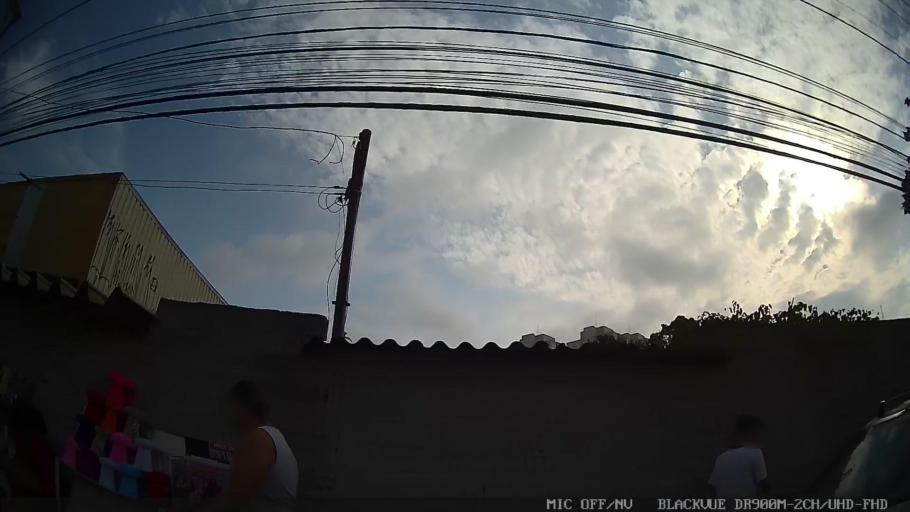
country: BR
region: Sao Paulo
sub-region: Ferraz De Vasconcelos
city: Ferraz de Vasconcelos
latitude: -23.5331
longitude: -46.4008
